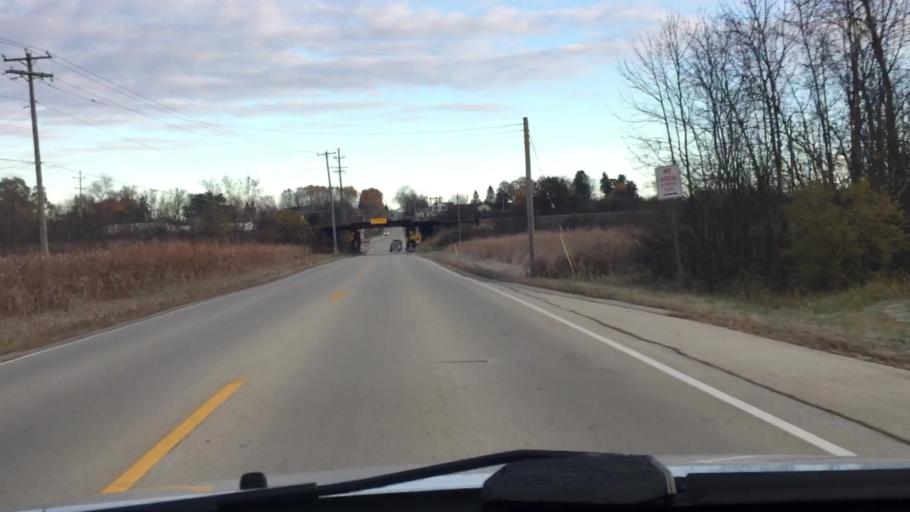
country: US
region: Wisconsin
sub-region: Waukesha County
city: Okauchee Lake
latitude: 43.1758
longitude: -88.4589
